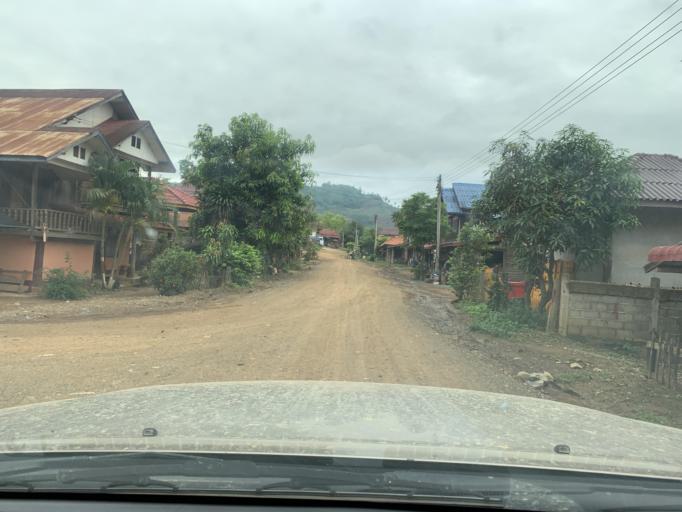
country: TH
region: Nan
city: Mae Charim
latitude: 18.4196
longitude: 101.4489
